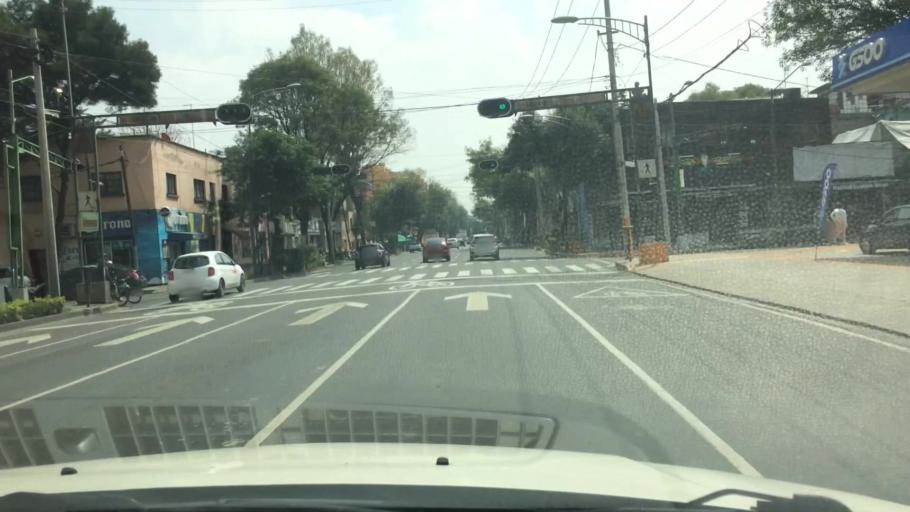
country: MX
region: Mexico City
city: Colonia Nativitas
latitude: 19.3788
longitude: -99.1455
